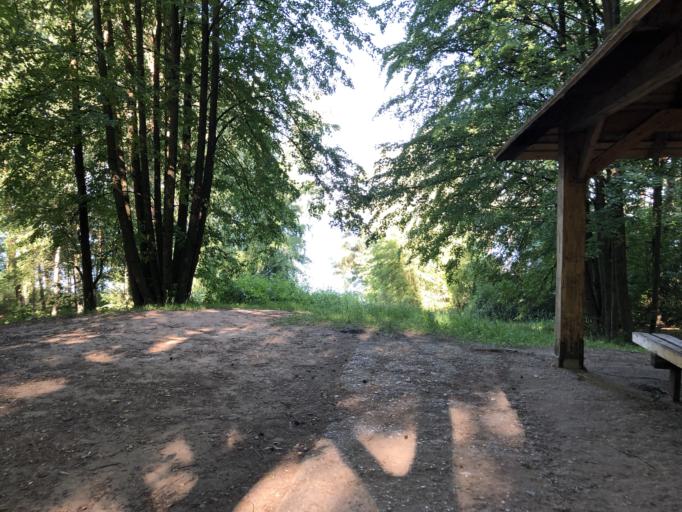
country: LT
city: Ramuciai
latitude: 54.8762
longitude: 24.0505
